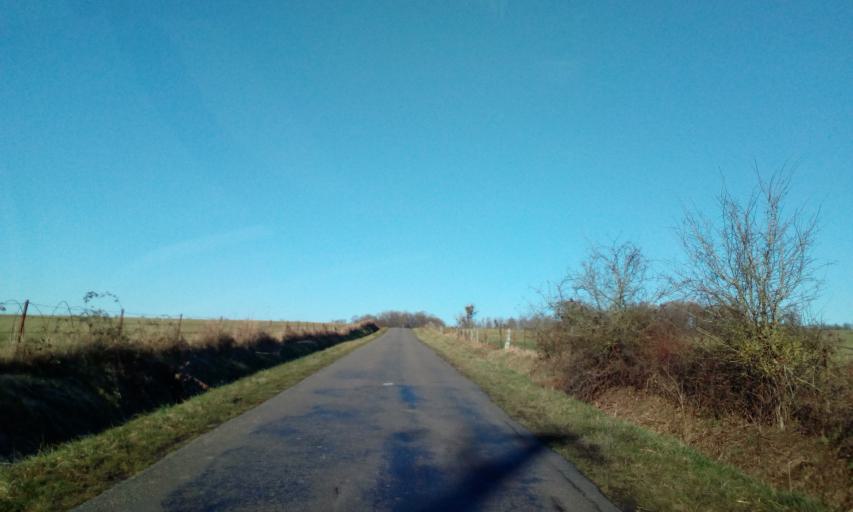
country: FR
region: Champagne-Ardenne
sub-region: Departement des Ardennes
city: Signy-le-Petit
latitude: 49.7344
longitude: 4.2978
